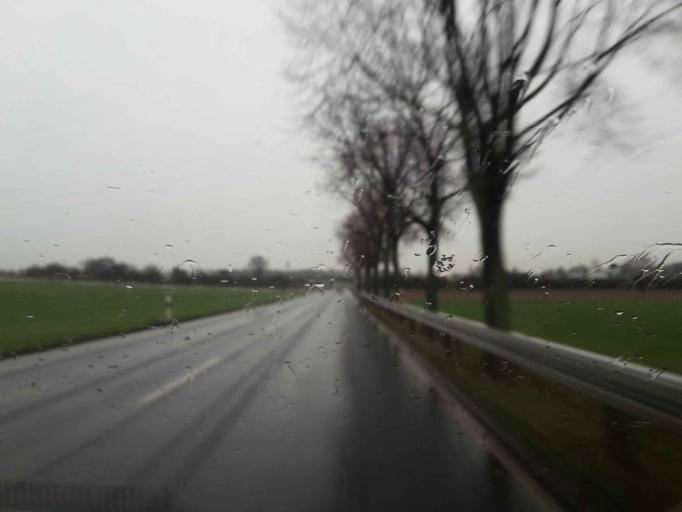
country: DE
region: Hesse
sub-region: Regierungsbezirk Darmstadt
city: Ober-Morlen
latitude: 50.3806
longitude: 8.7004
